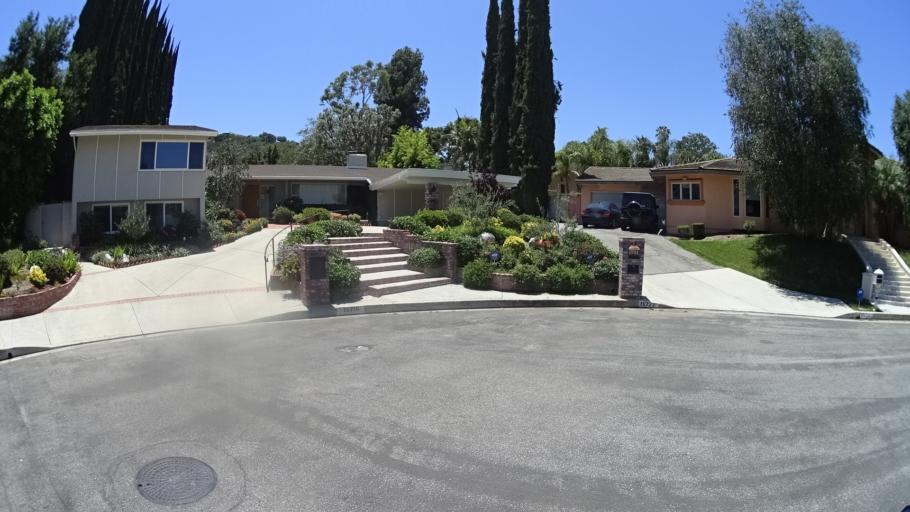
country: US
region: California
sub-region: Los Angeles County
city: Sherman Oaks
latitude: 34.1514
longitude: -118.4755
